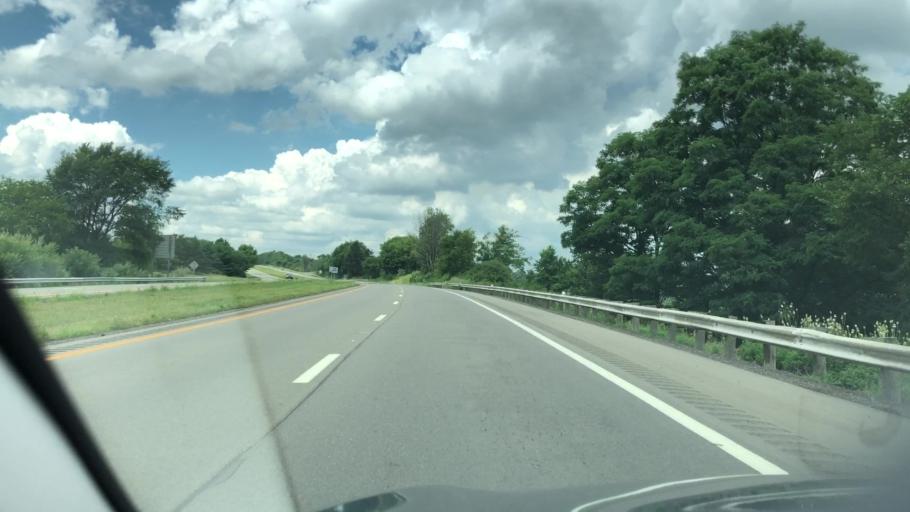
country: US
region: Ohio
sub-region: Stark County
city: Massillon
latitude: 40.8177
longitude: -81.5311
